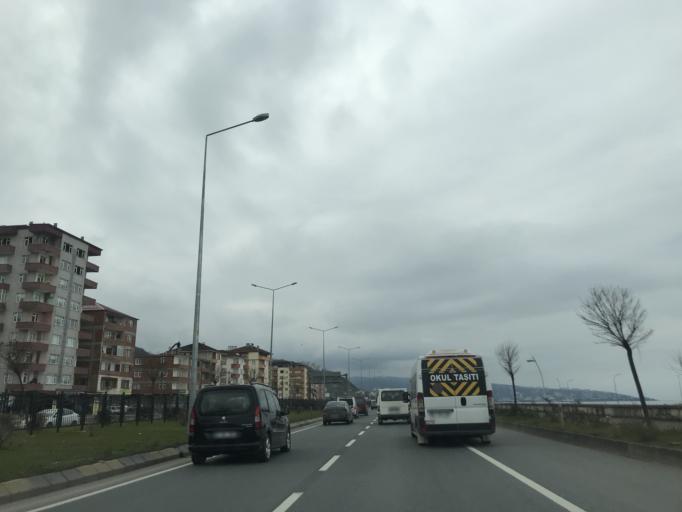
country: TR
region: Trabzon
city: Arsin
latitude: 40.9545
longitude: 39.9233
